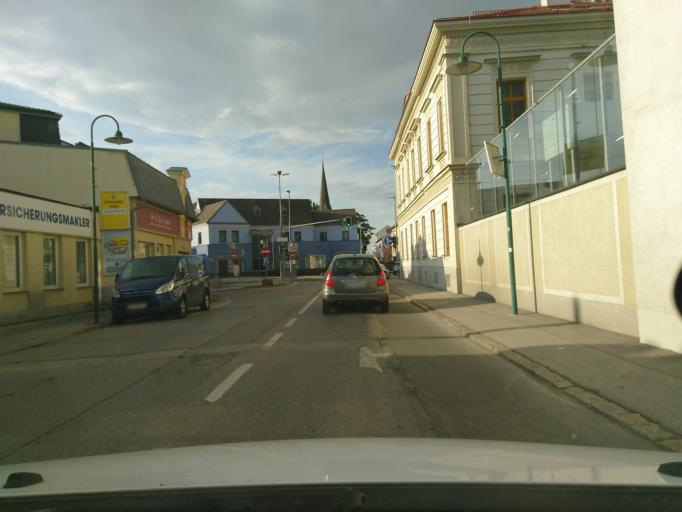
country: AT
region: Lower Austria
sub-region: Politischer Bezirk Modling
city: Brunn am Gebirge
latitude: 48.1049
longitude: 16.2853
